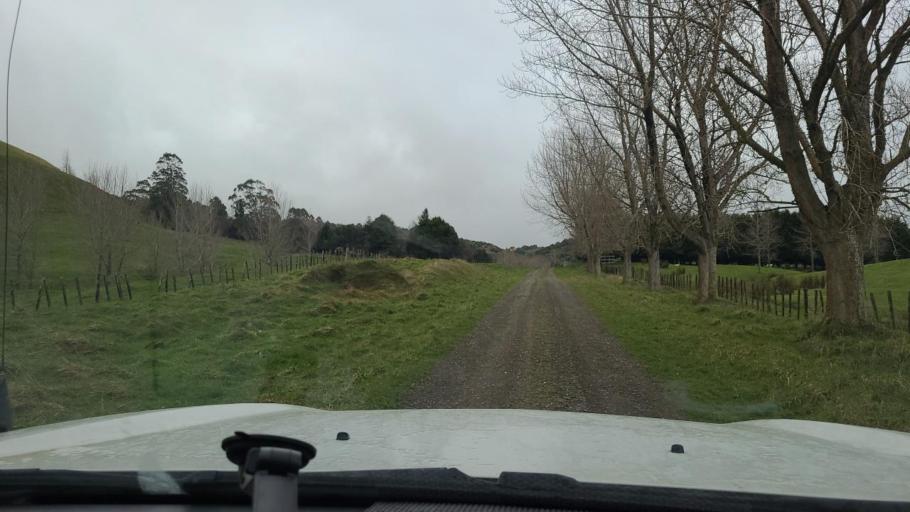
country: NZ
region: Hawke's Bay
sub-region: Wairoa District
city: Wairoa
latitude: -38.5418
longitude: 177.4129
